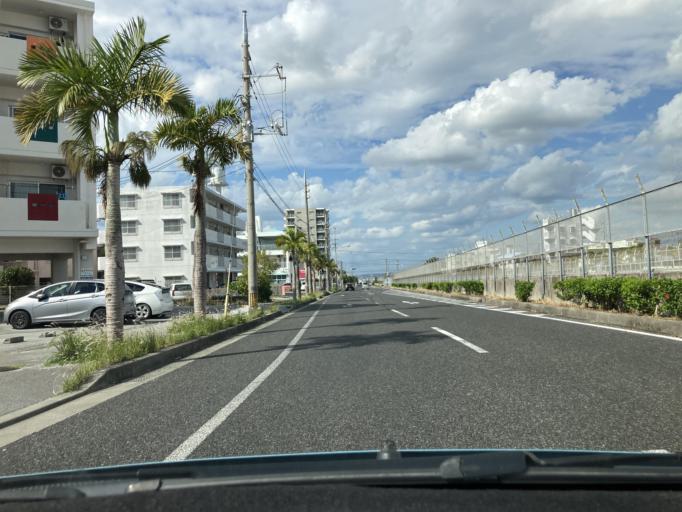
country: JP
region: Okinawa
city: Okinawa
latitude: 26.3240
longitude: 127.7880
